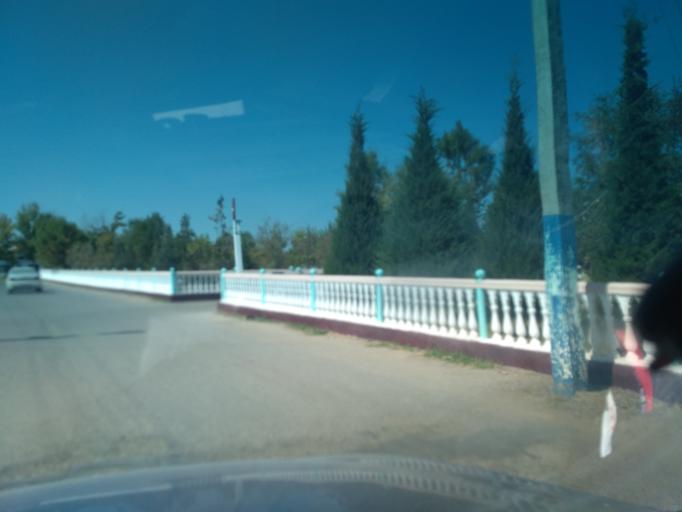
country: UZ
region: Sirdaryo
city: Guliston
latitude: 40.4960
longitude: 68.7017
